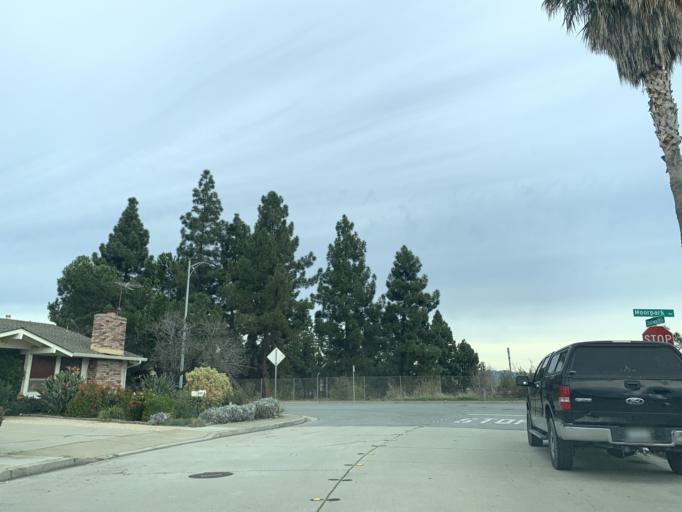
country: US
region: California
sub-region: Santa Clara County
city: Buena Vista
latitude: 37.3156
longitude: -121.9184
